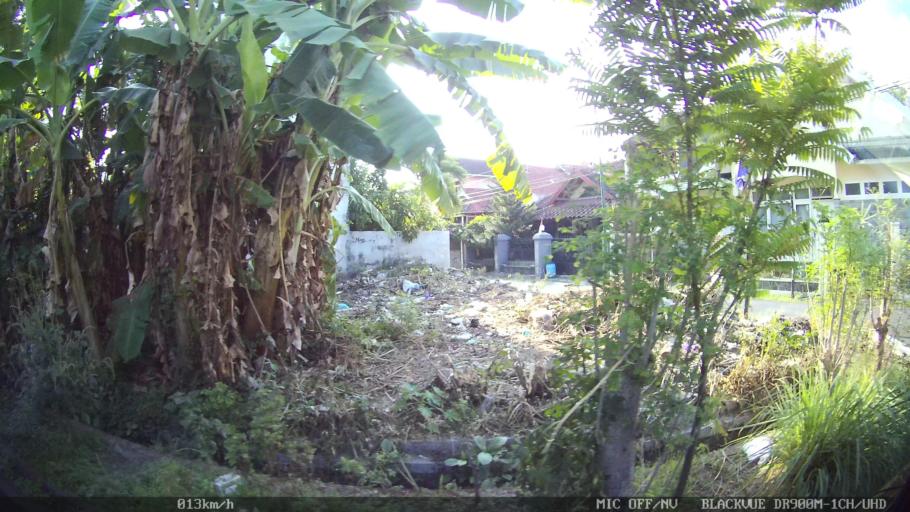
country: ID
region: Daerah Istimewa Yogyakarta
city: Yogyakarta
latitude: -7.8236
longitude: 110.3829
